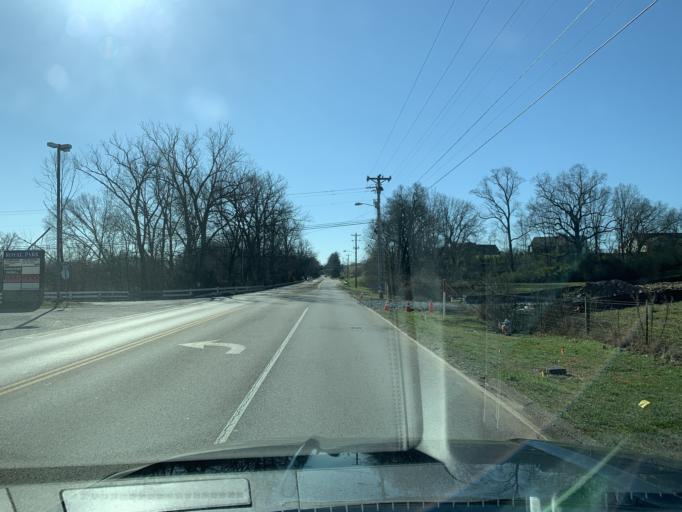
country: US
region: Tennessee
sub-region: Maury County
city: Spring Hill
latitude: 35.7281
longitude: -86.9246
